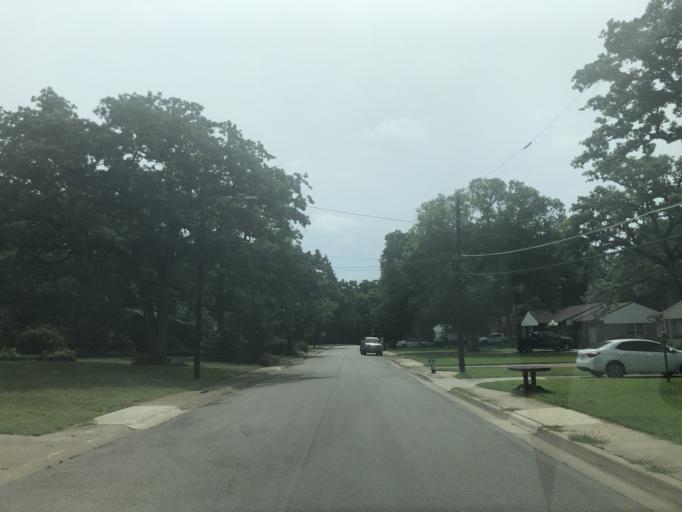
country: US
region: Texas
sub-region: Dallas County
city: Irving
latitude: 32.8060
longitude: -96.9683
